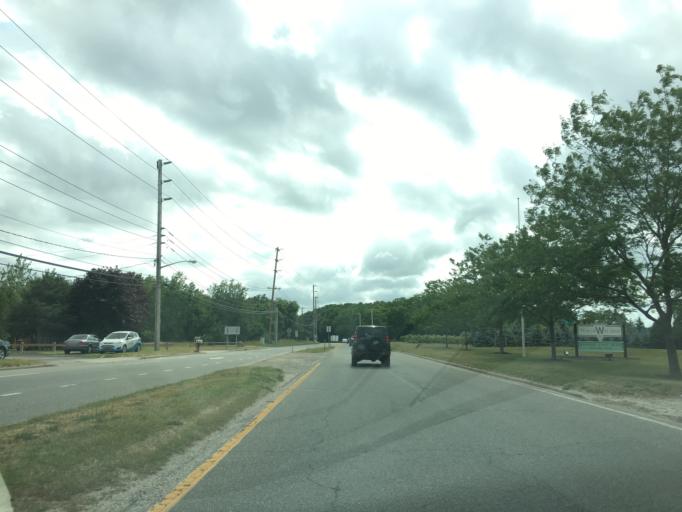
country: US
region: New York
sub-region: Suffolk County
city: Laurel
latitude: 40.9879
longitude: -72.5541
